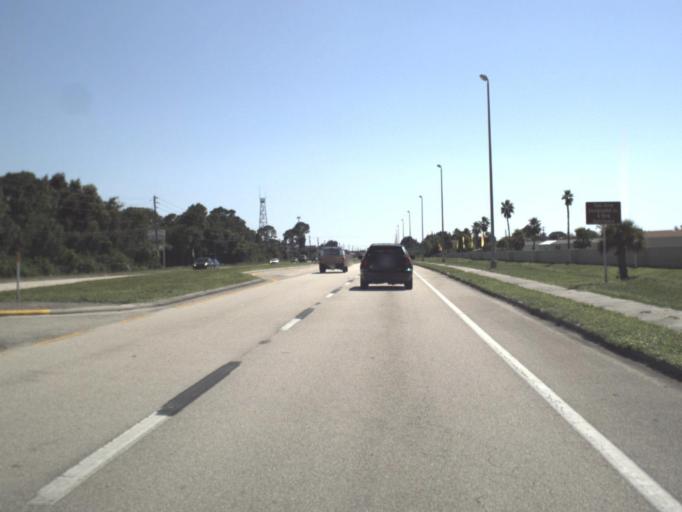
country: US
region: Florida
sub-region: Sarasota County
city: North Port
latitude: 26.9768
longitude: -82.2084
